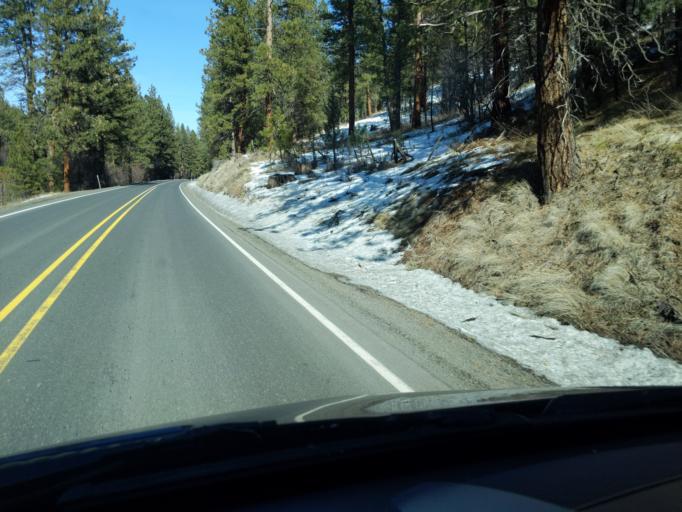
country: US
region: Oregon
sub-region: Grant County
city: John Day
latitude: 44.8718
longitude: -119.0211
